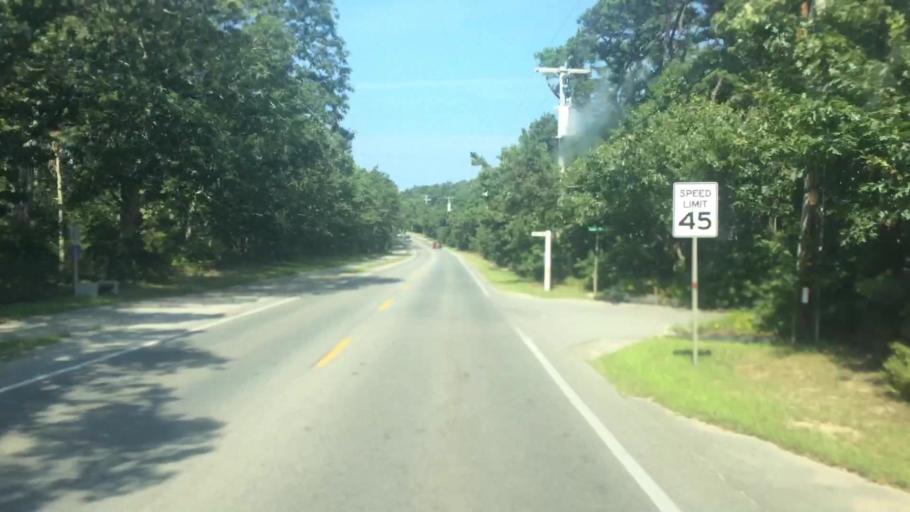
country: US
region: Massachusetts
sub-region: Dukes County
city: Oak Bluffs
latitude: 41.4134
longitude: -70.5776
